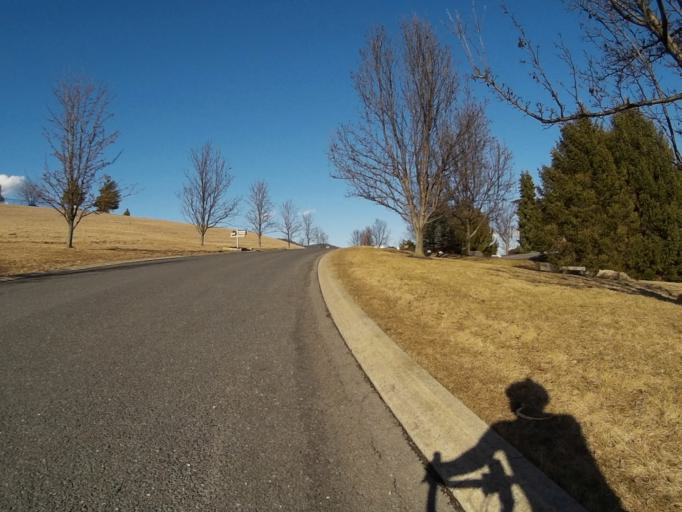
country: US
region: Pennsylvania
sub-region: Centre County
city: Park Forest Village
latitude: 40.8399
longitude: -77.9225
